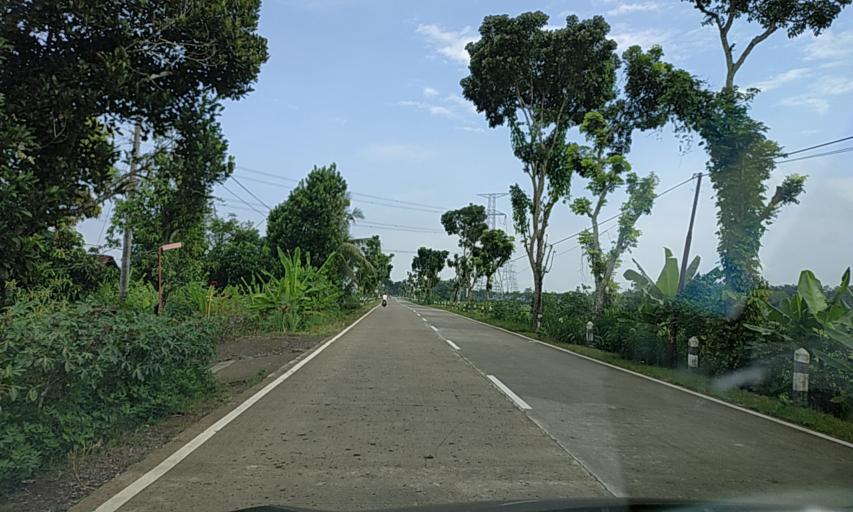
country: ID
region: Central Java
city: Tambangan
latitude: -7.4831
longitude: 108.8311
